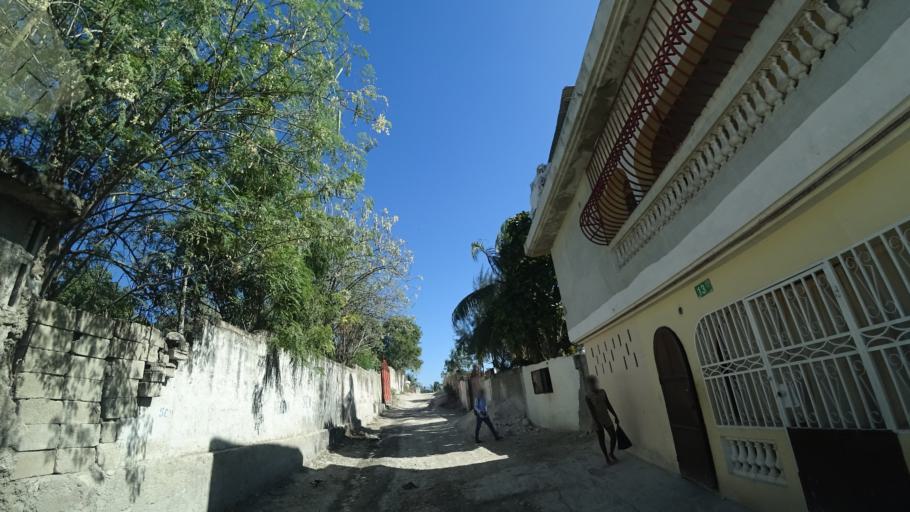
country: HT
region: Ouest
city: Delmas 73
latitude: 18.5578
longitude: -72.2871
